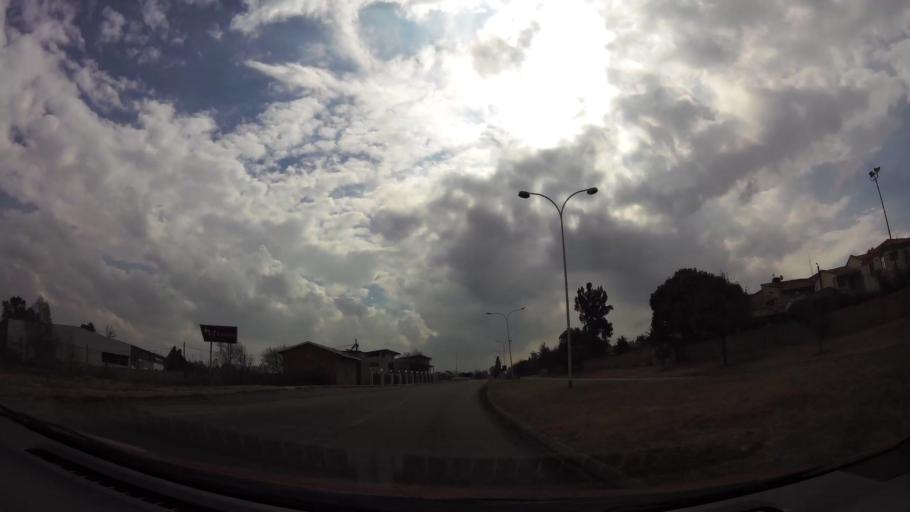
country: ZA
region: Gauteng
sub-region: Sedibeng District Municipality
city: Vanderbijlpark
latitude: -26.7419
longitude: 27.8447
